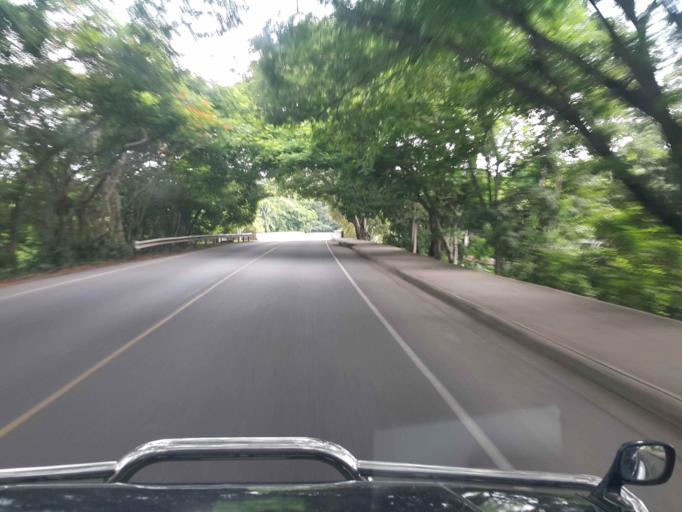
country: CR
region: Puntarenas
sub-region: Canton Central de Puntarenas
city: Chacarita
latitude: 9.9618
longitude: -84.7362
